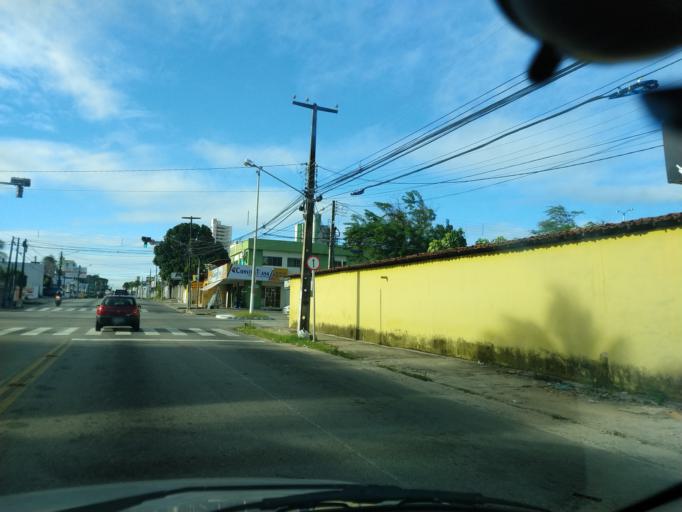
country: BR
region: Rio Grande do Norte
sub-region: Natal
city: Natal
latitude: -5.8239
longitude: -35.2201
